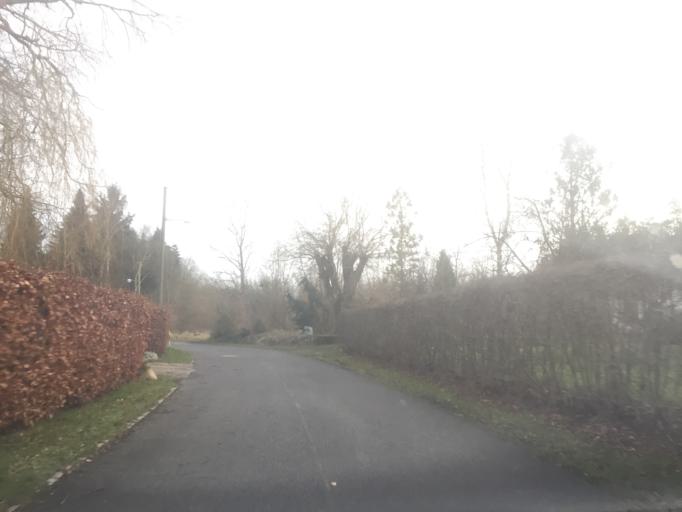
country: DK
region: Capital Region
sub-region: Hoje-Taastrup Kommune
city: Taastrup
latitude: 55.6883
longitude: 12.3252
